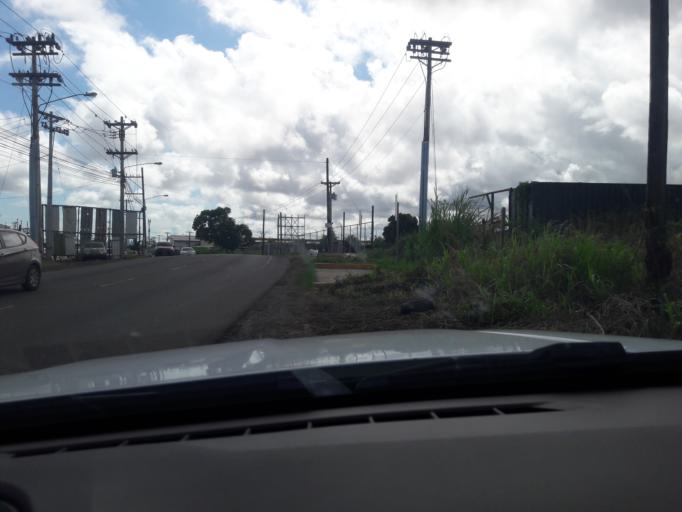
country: PA
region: Panama
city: Tocumen
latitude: 9.0790
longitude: -79.4096
